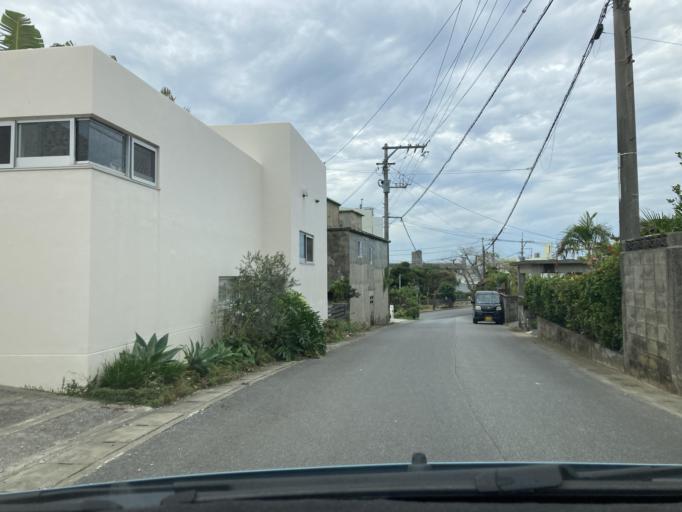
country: JP
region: Okinawa
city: Ishikawa
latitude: 26.4041
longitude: 127.7392
